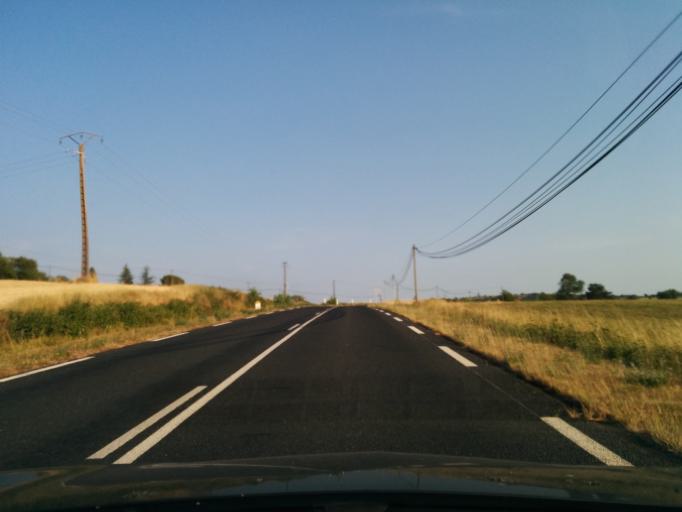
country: FR
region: Midi-Pyrenees
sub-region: Departement du Lot
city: Le Vigan
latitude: 44.7507
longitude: 1.4986
